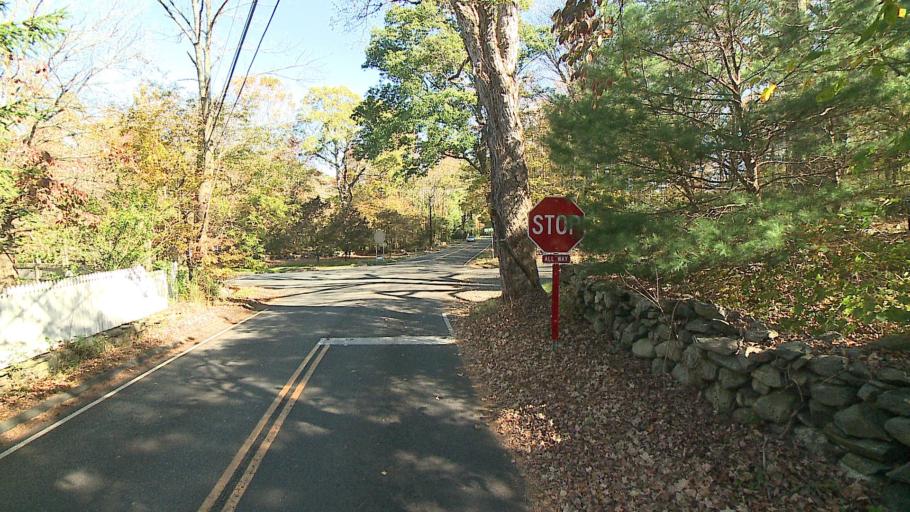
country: US
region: Connecticut
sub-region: Fairfield County
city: Westport
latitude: 41.2200
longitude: -73.3246
